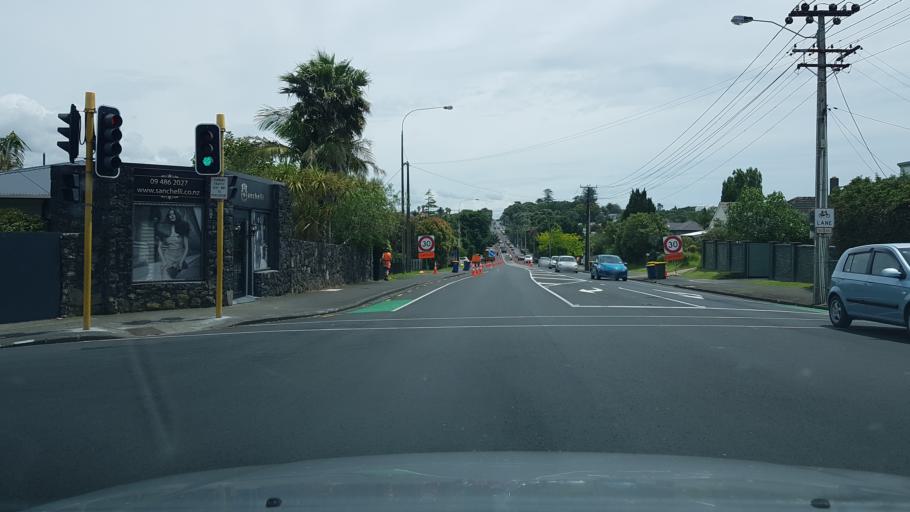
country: NZ
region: Auckland
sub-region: Auckland
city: North Shore
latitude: -36.8052
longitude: 174.7886
